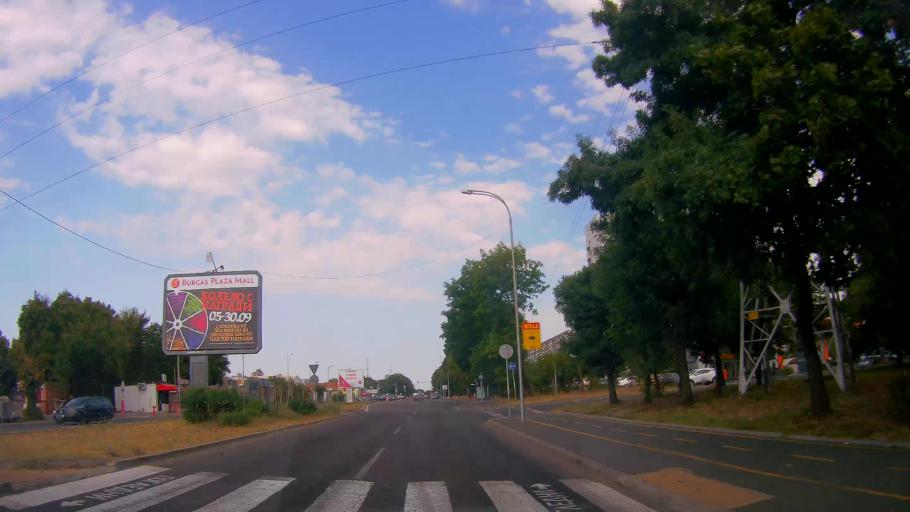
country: BG
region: Burgas
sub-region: Obshtina Burgas
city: Burgas
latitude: 42.5158
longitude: 27.4503
